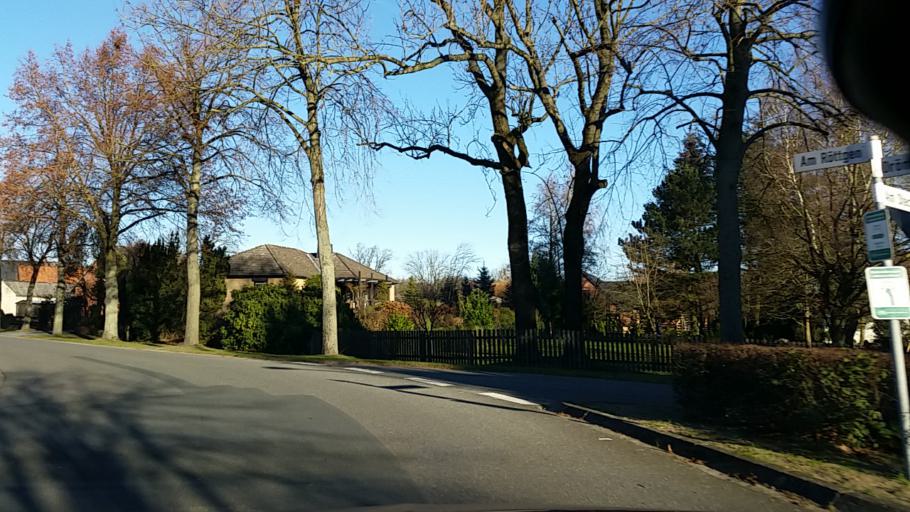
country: DE
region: Lower Saxony
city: Brome
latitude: 52.5704
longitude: 10.9369
